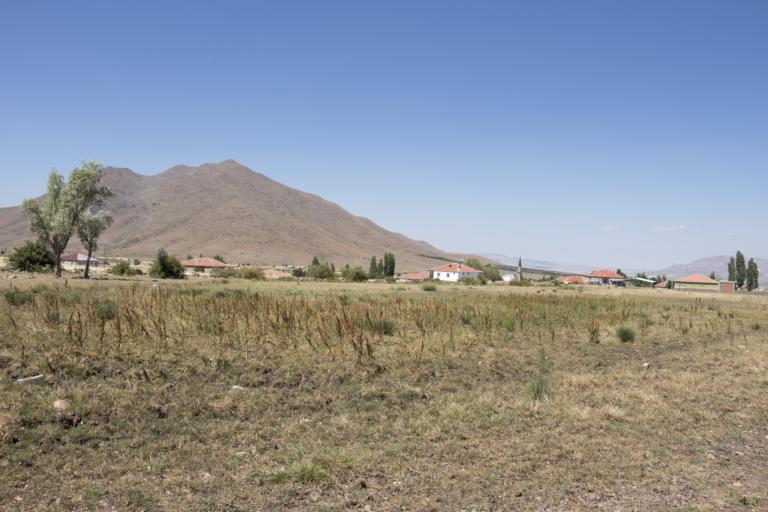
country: TR
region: Kayseri
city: Toklar
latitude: 38.4074
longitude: 36.0870
